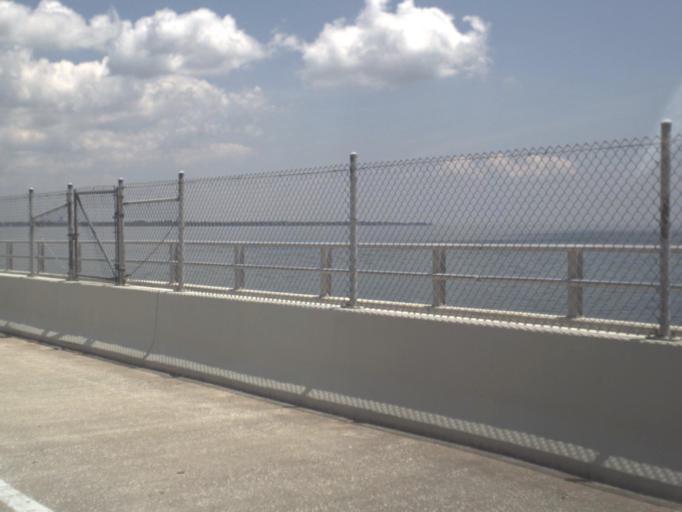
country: US
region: Florida
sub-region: Pinellas County
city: Tierra Verde
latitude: 27.6623
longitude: -82.6772
